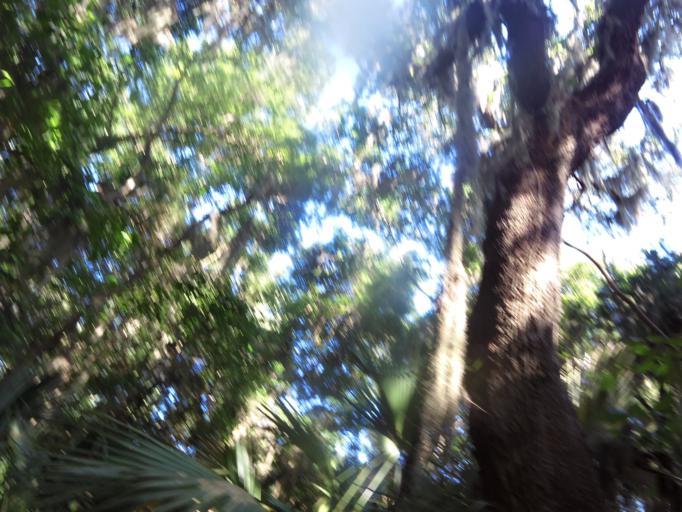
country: US
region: Florida
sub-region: Duval County
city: Atlantic Beach
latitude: 30.4366
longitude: -81.4717
